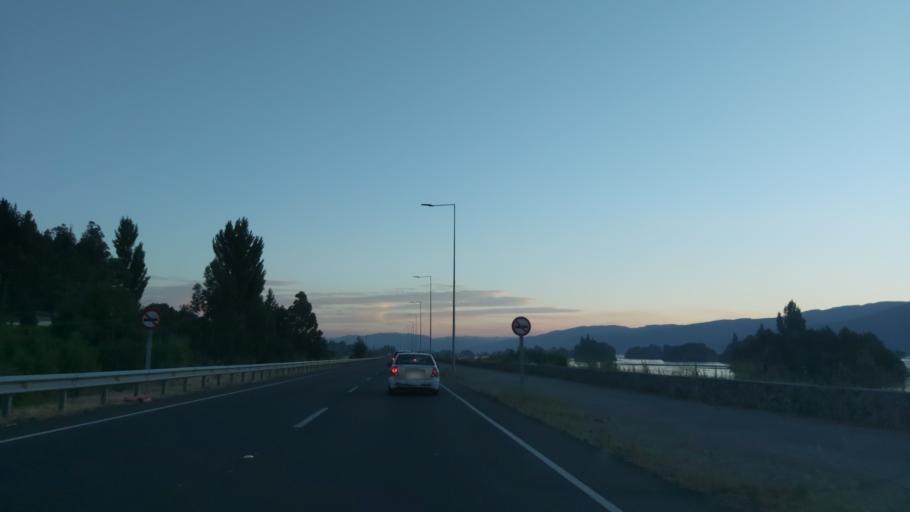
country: CL
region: Biobio
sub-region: Provincia de Concepcion
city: Chiguayante
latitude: -36.8844
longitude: -73.0385
